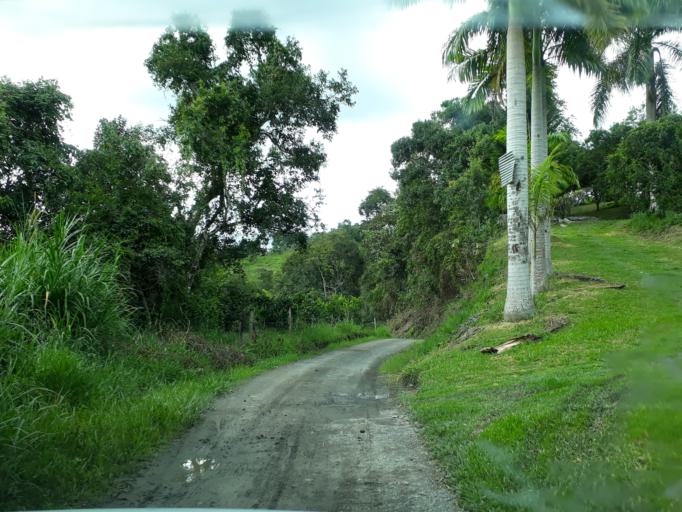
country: CO
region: Cundinamarca
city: Pacho
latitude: 5.1781
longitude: -74.2481
